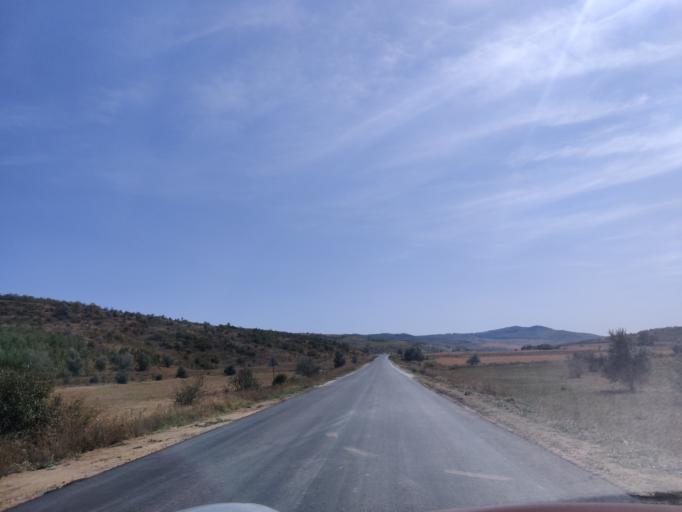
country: MD
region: Ungheni
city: Ungheni
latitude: 47.2512
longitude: 27.9989
